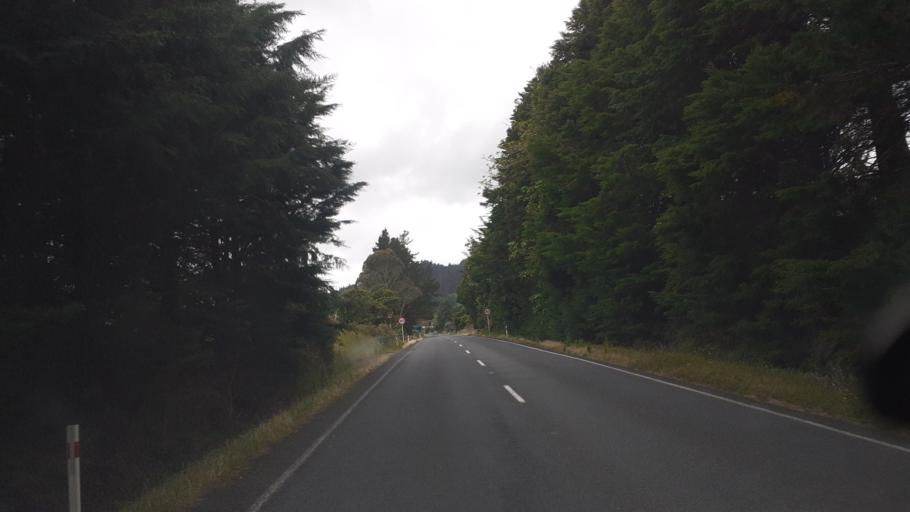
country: NZ
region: Northland
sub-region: Far North District
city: Waimate North
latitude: -35.3036
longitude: 173.9544
